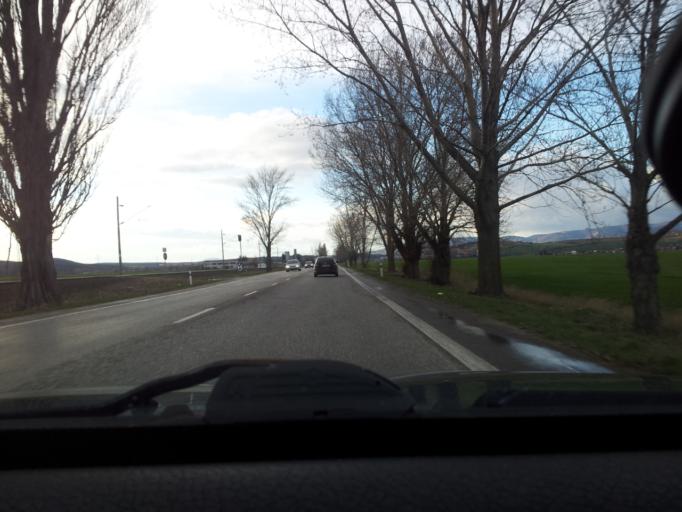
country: SK
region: Nitriansky
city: Tlmace
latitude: 48.2710
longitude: 18.5597
